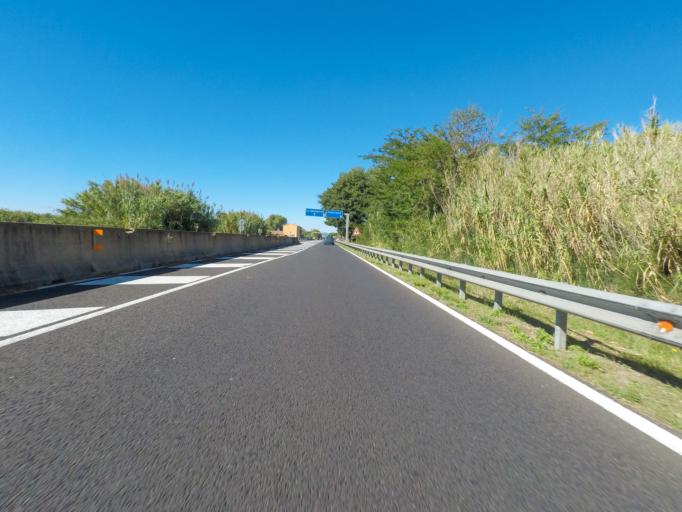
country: IT
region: Tuscany
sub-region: Provincia di Grosseto
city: Orbetello Scalo
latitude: 42.4703
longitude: 11.2370
